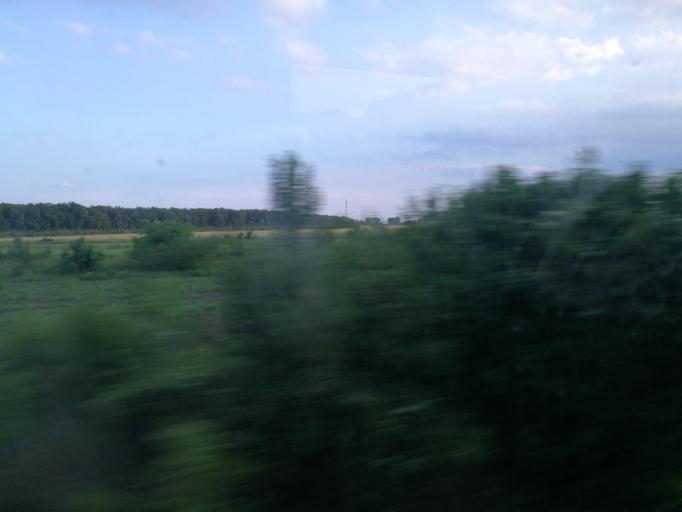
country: RO
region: Dambovita
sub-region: Comuna Contesti
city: Contesti
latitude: 44.6602
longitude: 25.6279
